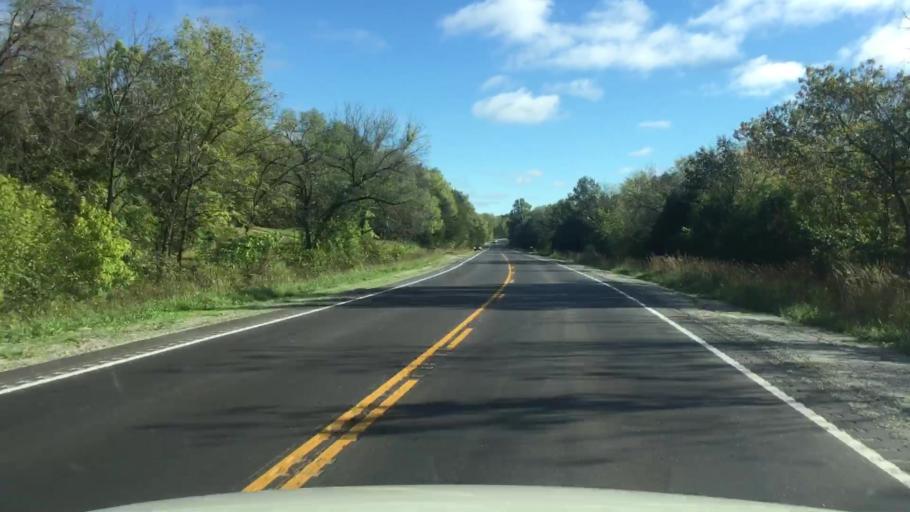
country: US
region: Missouri
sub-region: Howard County
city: New Franklin
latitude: 38.9856
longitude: -92.5400
